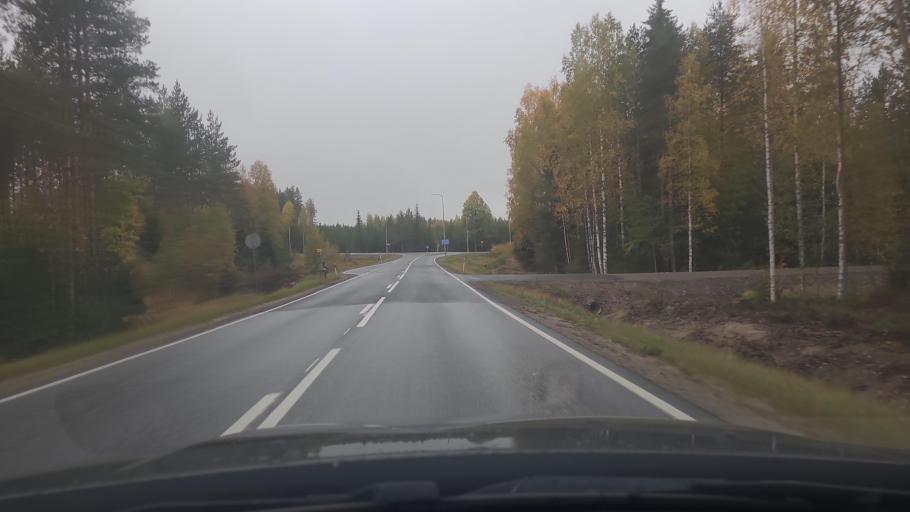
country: FI
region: Northern Savo
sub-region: Varkaus
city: Kangaslampi
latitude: 62.4604
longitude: 28.3203
